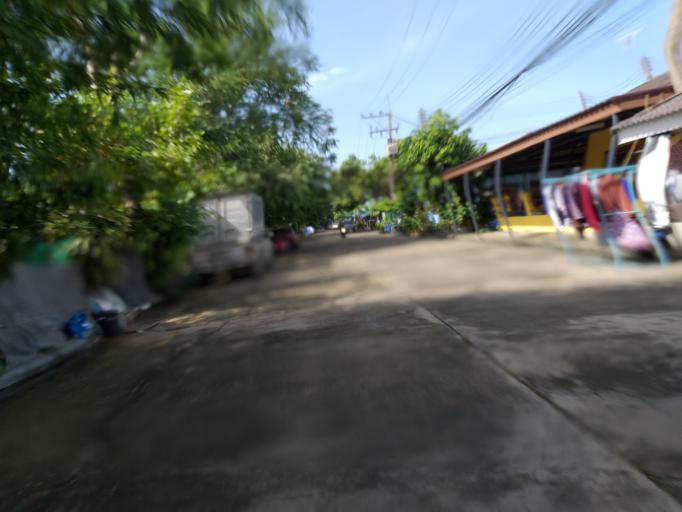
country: TH
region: Pathum Thani
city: Nong Suea
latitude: 14.0553
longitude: 100.8553
